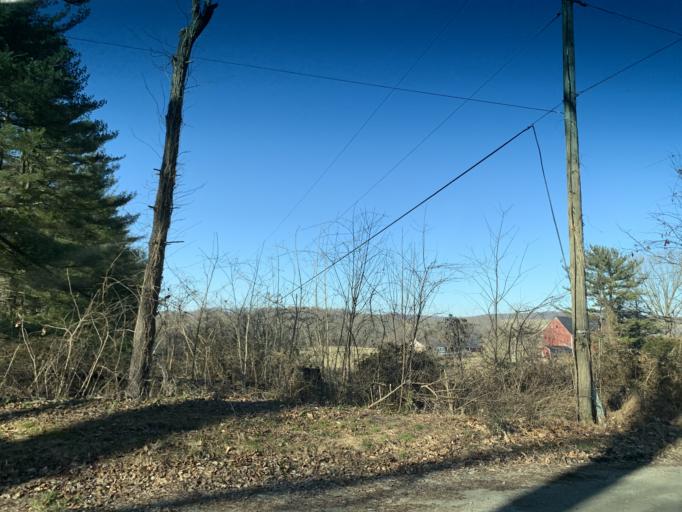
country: US
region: Maryland
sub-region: Harford County
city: Aberdeen
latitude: 39.6072
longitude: -76.2339
